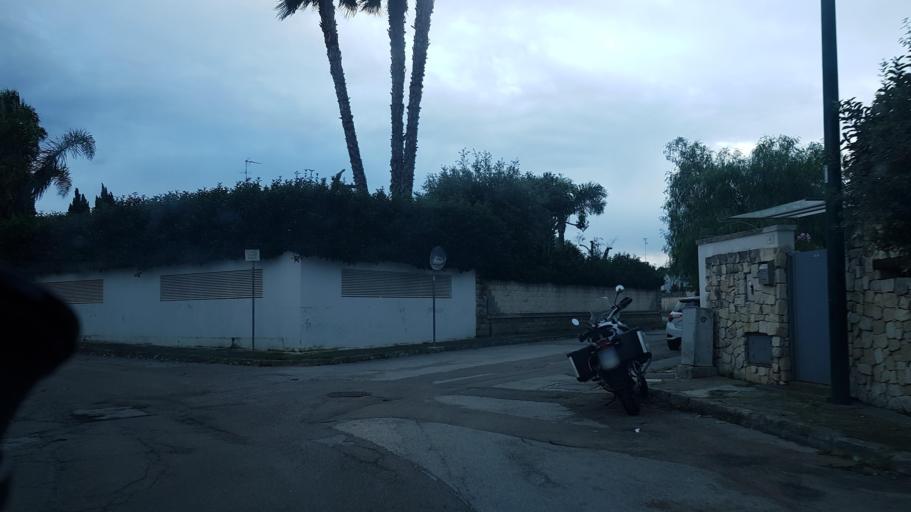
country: IT
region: Apulia
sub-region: Provincia di Lecce
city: Merine
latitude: 40.3403
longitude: 18.2171
